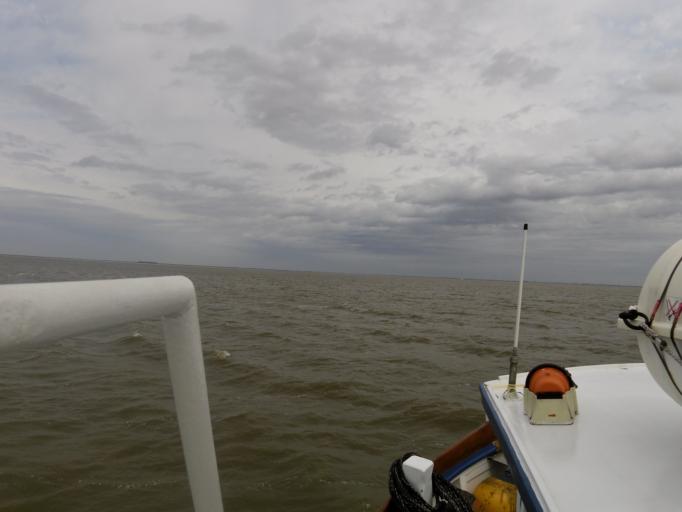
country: DE
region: Schleswig-Holstein
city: Grode
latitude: 54.6282
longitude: 8.6755
